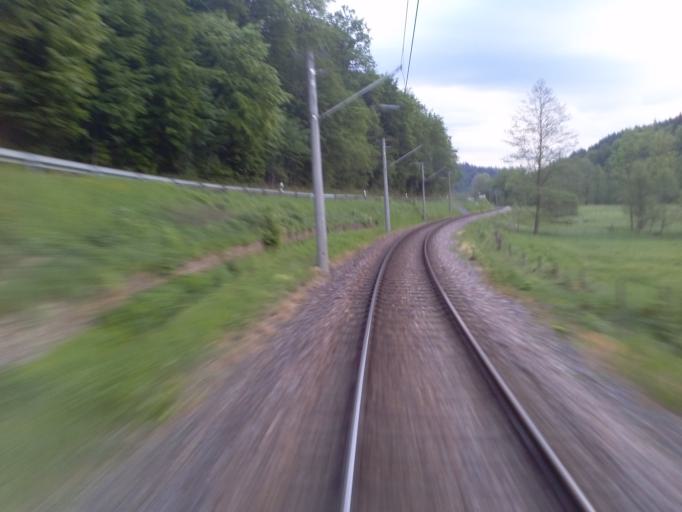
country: DE
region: Baden-Wuerttemberg
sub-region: Karlsruhe Region
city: Ettlingen
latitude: 48.8853
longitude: 8.4520
